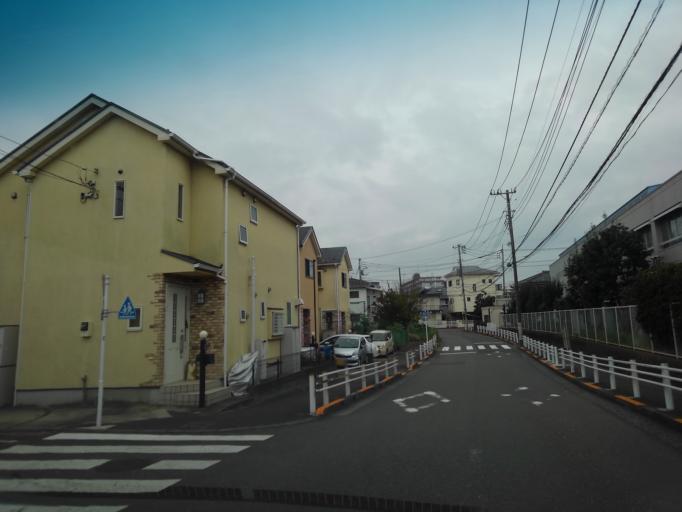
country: JP
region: Tokyo
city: Chofugaoka
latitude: 35.6439
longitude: 139.5212
